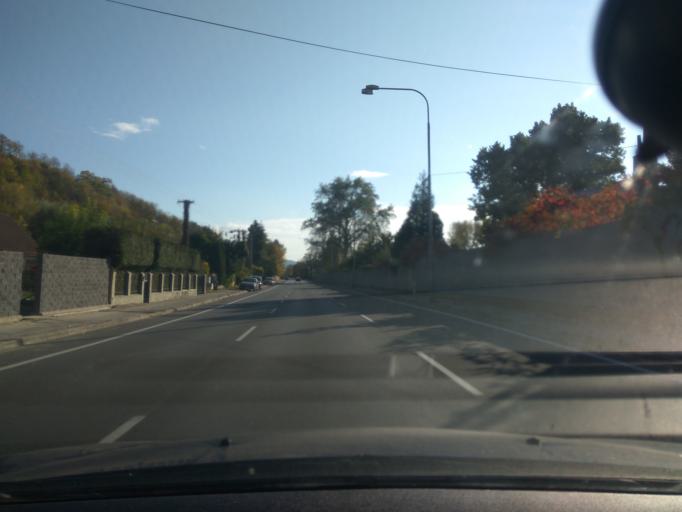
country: SK
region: Trnavsky
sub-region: Okres Trnava
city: Piestany
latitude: 48.5787
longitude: 17.8347
